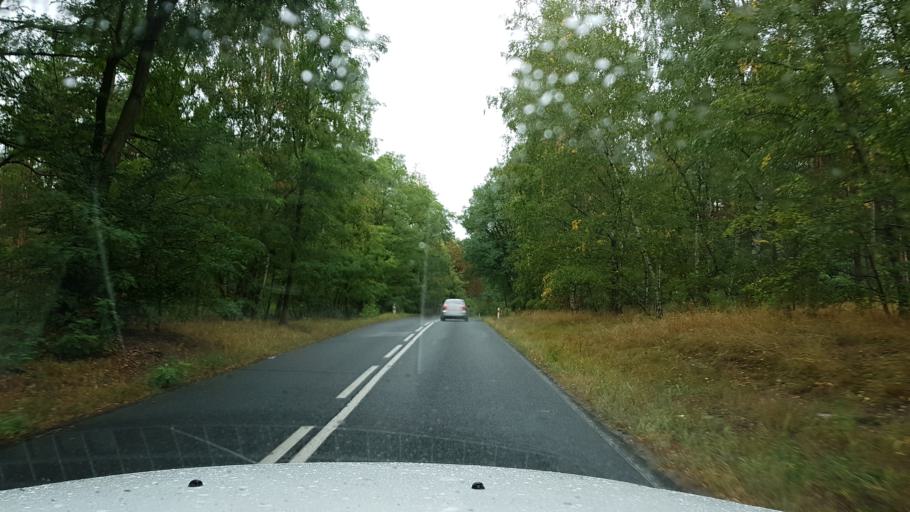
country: PL
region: West Pomeranian Voivodeship
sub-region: Powiat gryfinski
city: Cedynia
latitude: 52.8370
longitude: 14.1275
